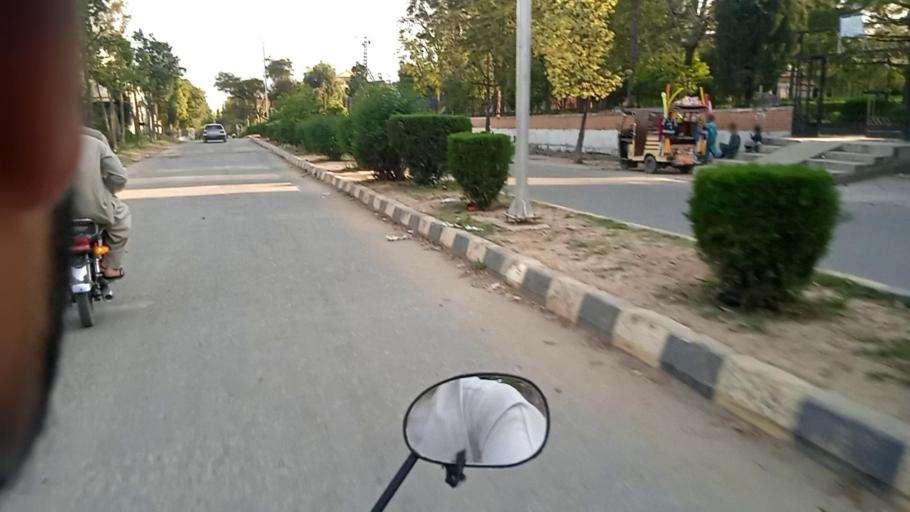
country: PK
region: Khyber Pakhtunkhwa
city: Mingora
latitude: 34.8315
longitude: 72.3423
